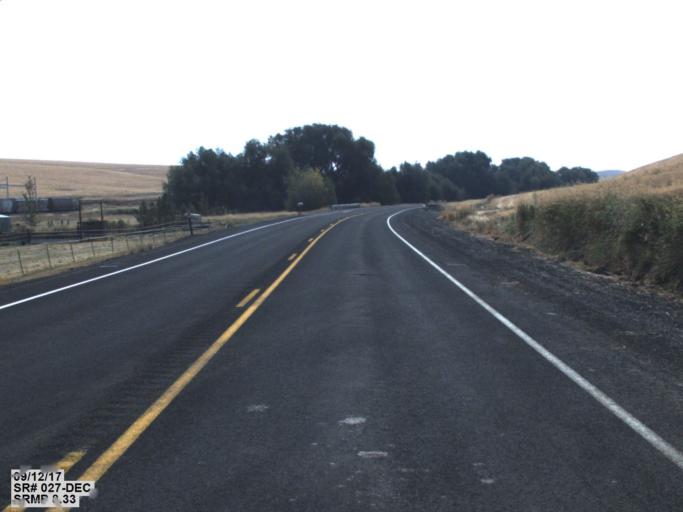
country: US
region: Washington
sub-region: Whitman County
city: Pullman
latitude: 46.8351
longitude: -117.1180
